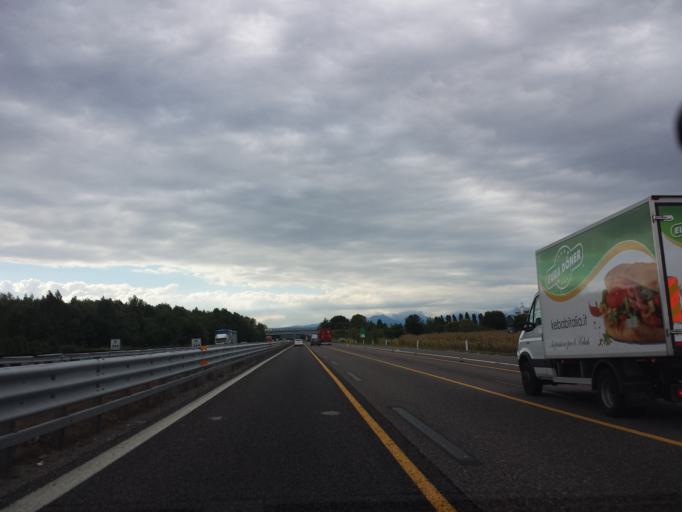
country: IT
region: Veneto
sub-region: Provincia di Vicenza
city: Grumolo delle Abbadesse
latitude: 45.4908
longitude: 11.6686
